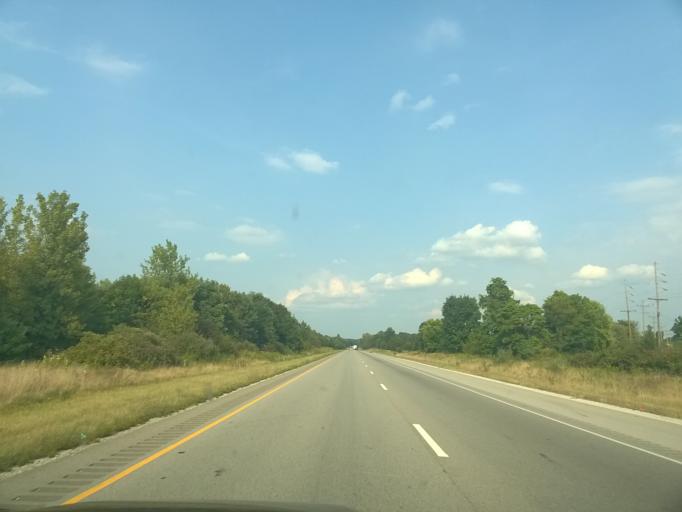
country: US
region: Indiana
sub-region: Vigo County
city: Seelyville
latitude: 39.4342
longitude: -87.2908
